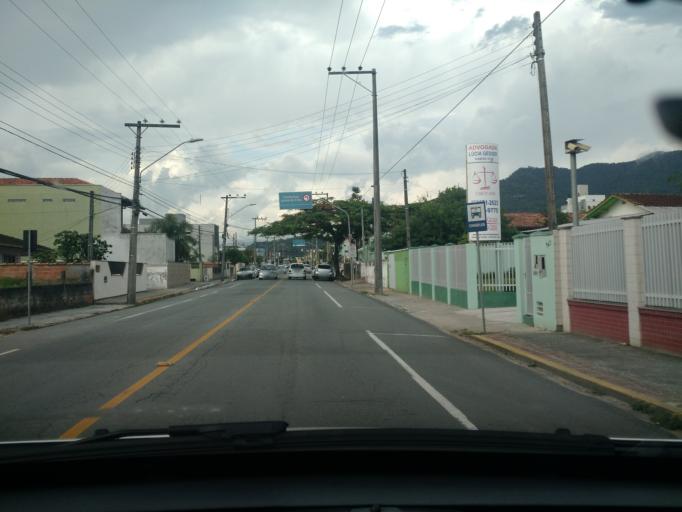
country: BR
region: Santa Catarina
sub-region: Jaragua Do Sul
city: Jaragua do Sul
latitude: -26.4853
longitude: -49.0924
